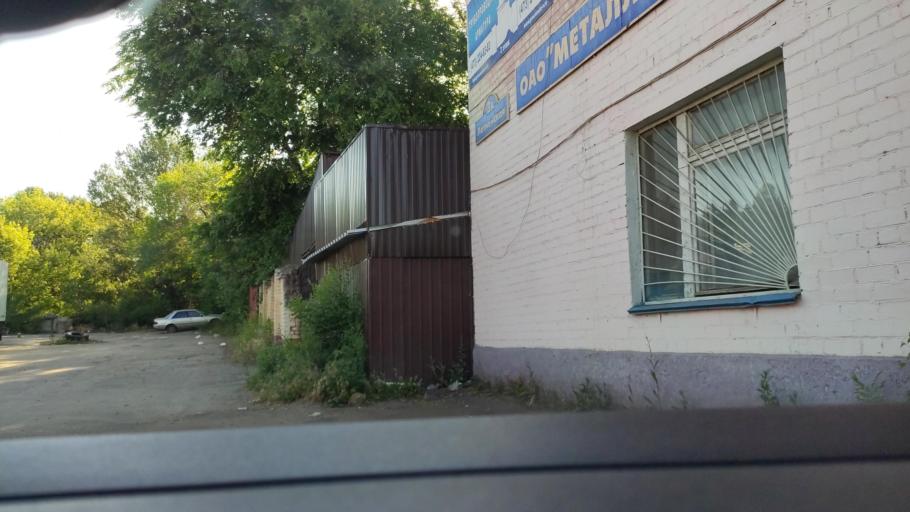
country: RU
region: Voronezj
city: Pridonskoy
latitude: 51.6753
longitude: 39.0862
